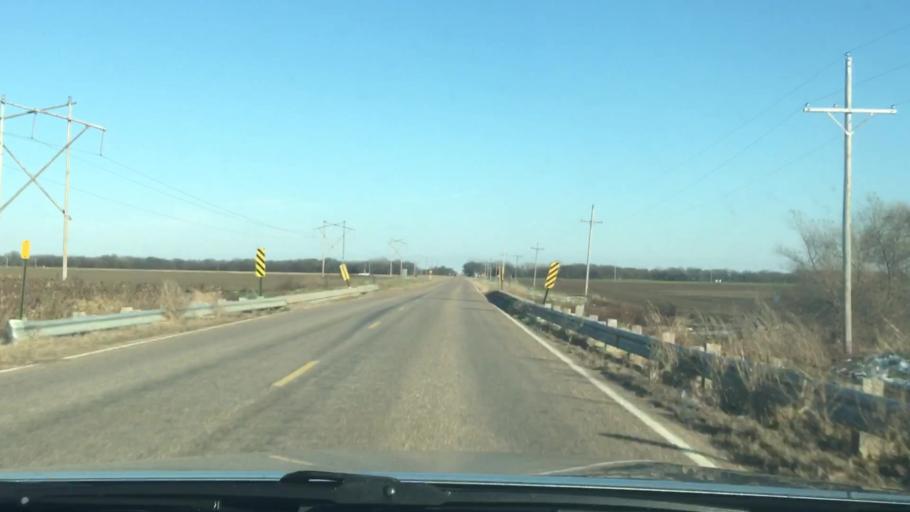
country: US
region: Kansas
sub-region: Rice County
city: Lyons
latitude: 38.2895
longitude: -98.1335
